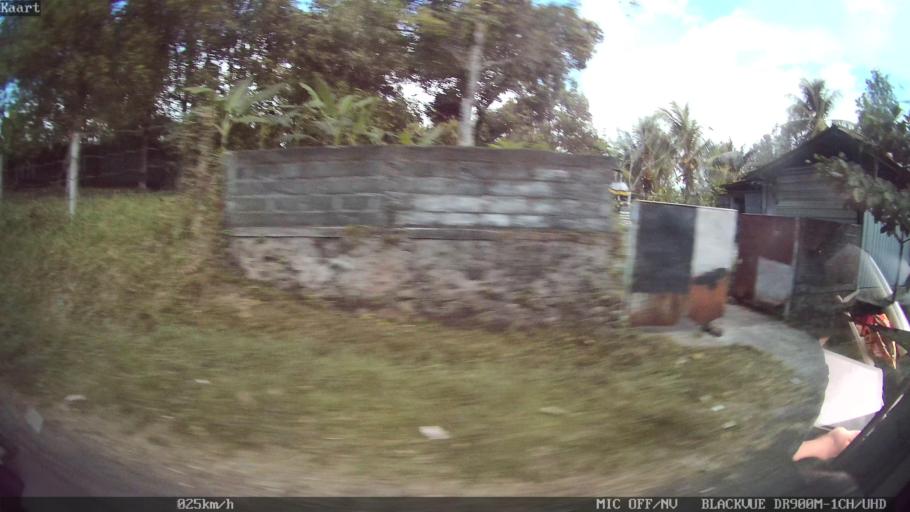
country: ID
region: Bali
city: Kauhan
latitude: -8.2639
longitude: 114.9697
